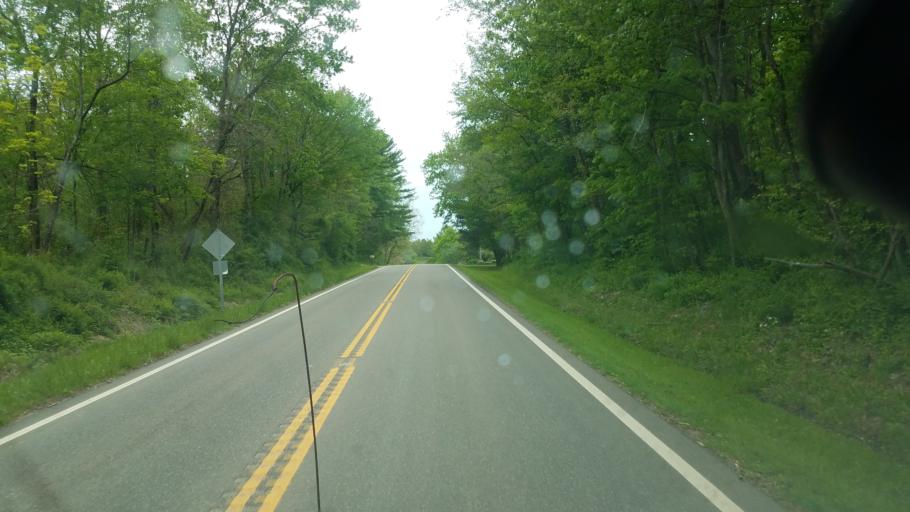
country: US
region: Ohio
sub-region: Tuscarawas County
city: Newcomerstown
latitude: 40.1635
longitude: -81.5347
